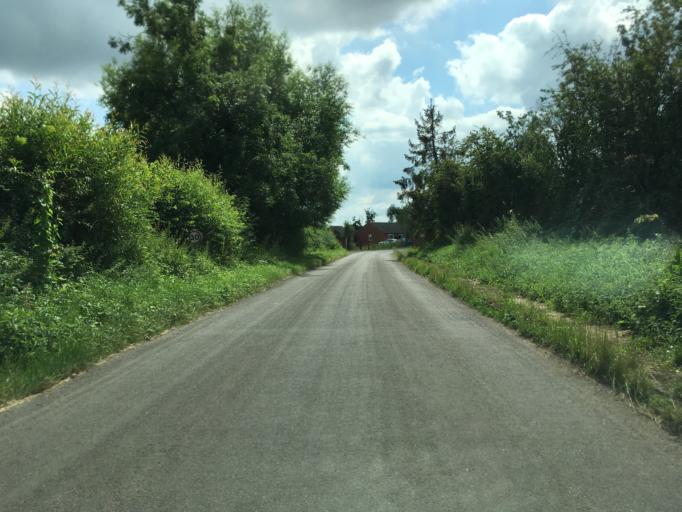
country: GB
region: England
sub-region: Gloucestershire
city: Gloucester
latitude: 51.9005
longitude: -2.2516
